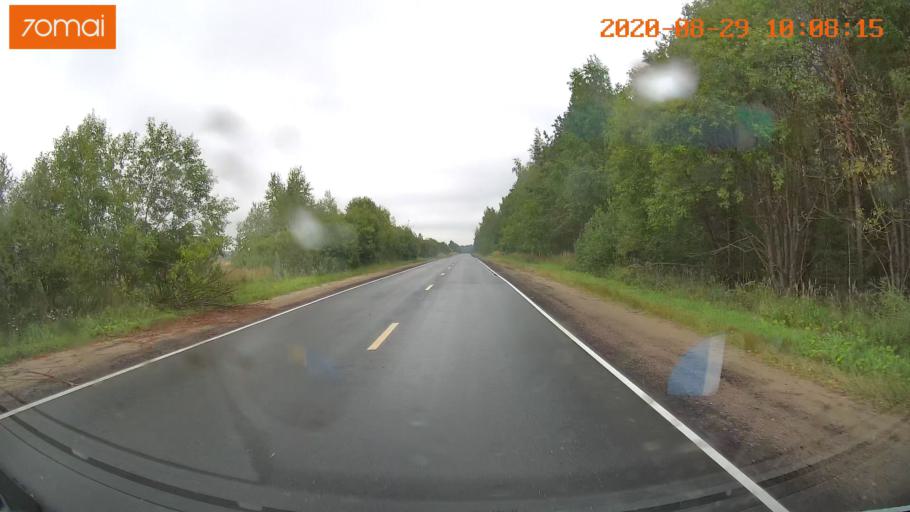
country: RU
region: Ivanovo
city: Kuznechikha
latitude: 57.3766
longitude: 42.5852
